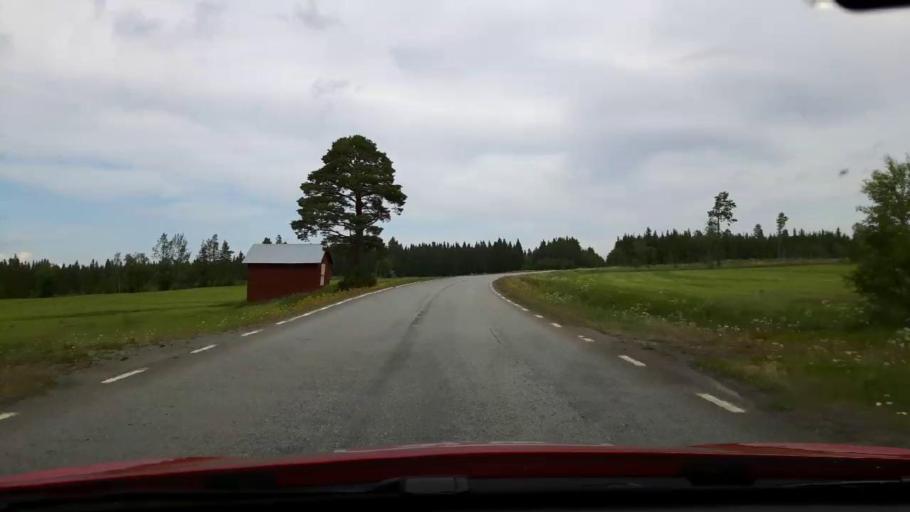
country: SE
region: Jaemtland
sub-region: OEstersunds Kommun
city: Ostersund
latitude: 63.0630
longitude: 14.4474
